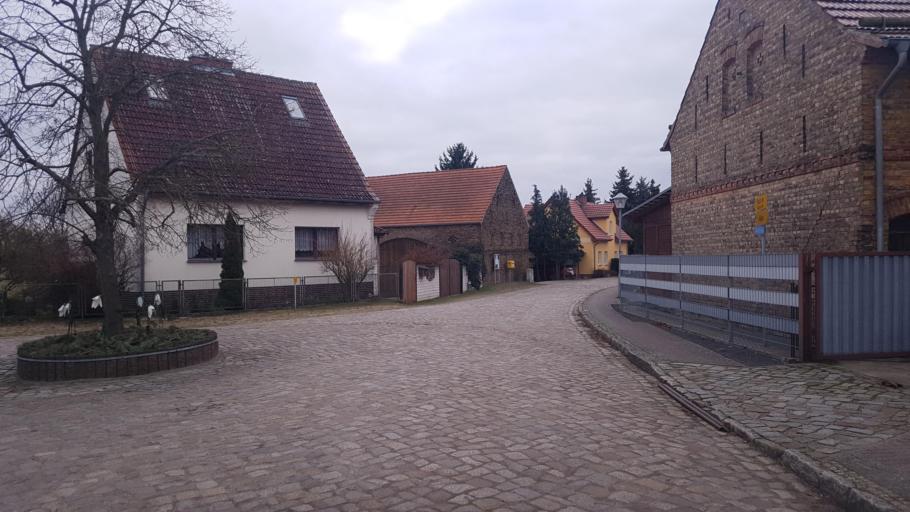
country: DE
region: Brandenburg
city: Halbe
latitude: 52.0690
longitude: 13.6975
